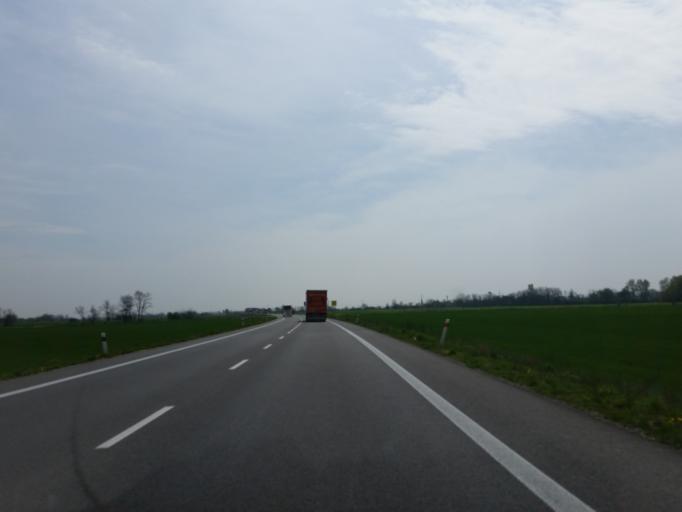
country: SK
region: Trnavsky
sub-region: Okres Galanta
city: Galanta
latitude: 48.2136
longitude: 17.7372
